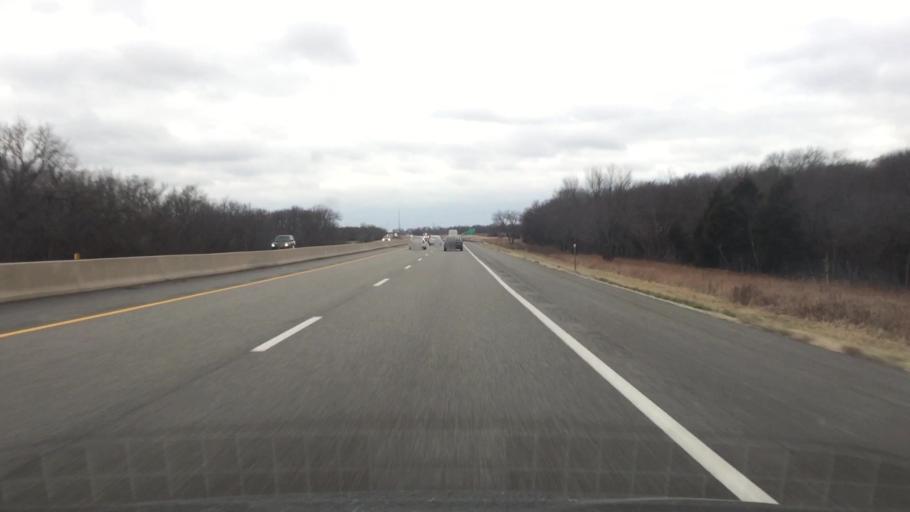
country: US
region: Kansas
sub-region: Butler County
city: Andover
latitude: 37.7307
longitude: -97.0879
